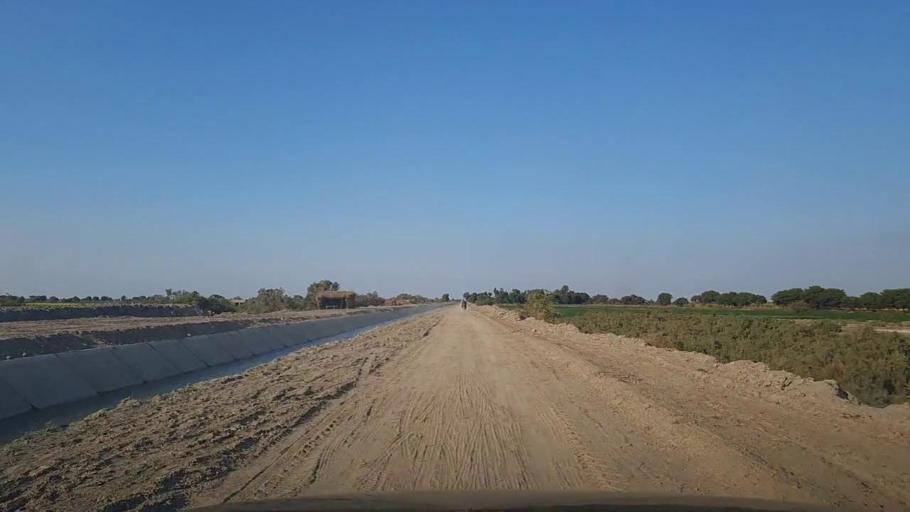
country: PK
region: Sindh
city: Jhol
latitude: 25.8920
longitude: 69.0383
